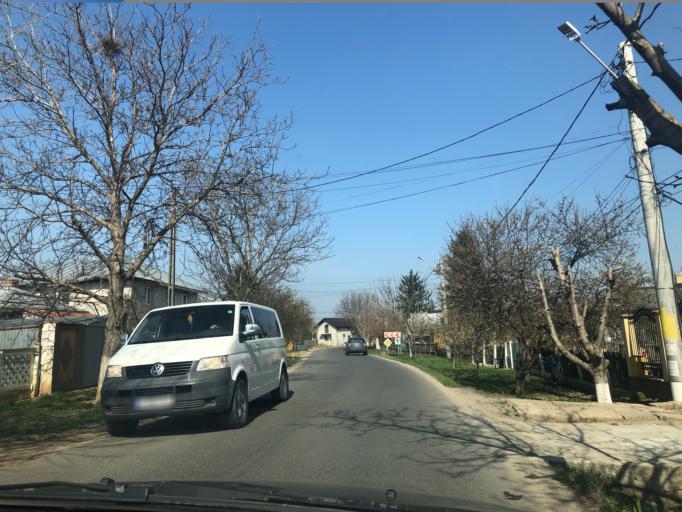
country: RO
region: Ilfov
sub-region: Comuna Clinceni
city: Clinceni
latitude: 44.3764
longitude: 25.9525
